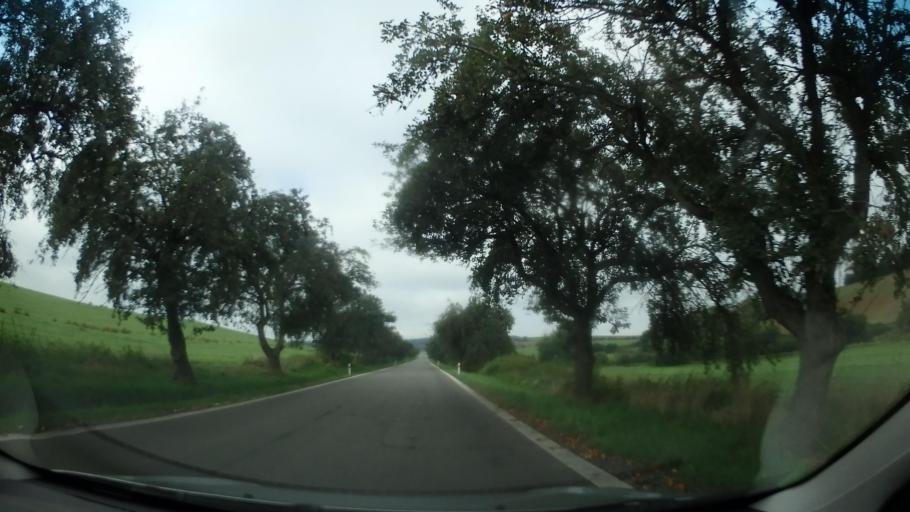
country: CZ
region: Central Bohemia
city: Neveklov
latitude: 49.7534
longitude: 14.5929
